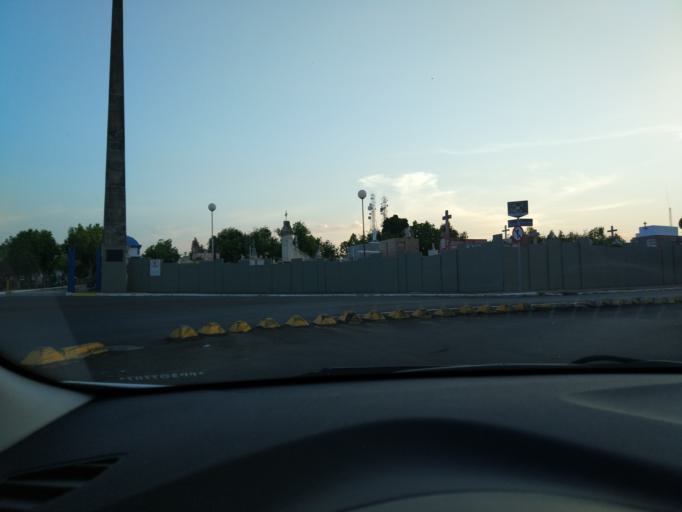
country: BR
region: Sao Paulo
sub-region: Botucatu
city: Botucatu
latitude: -22.8967
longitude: -48.4455
